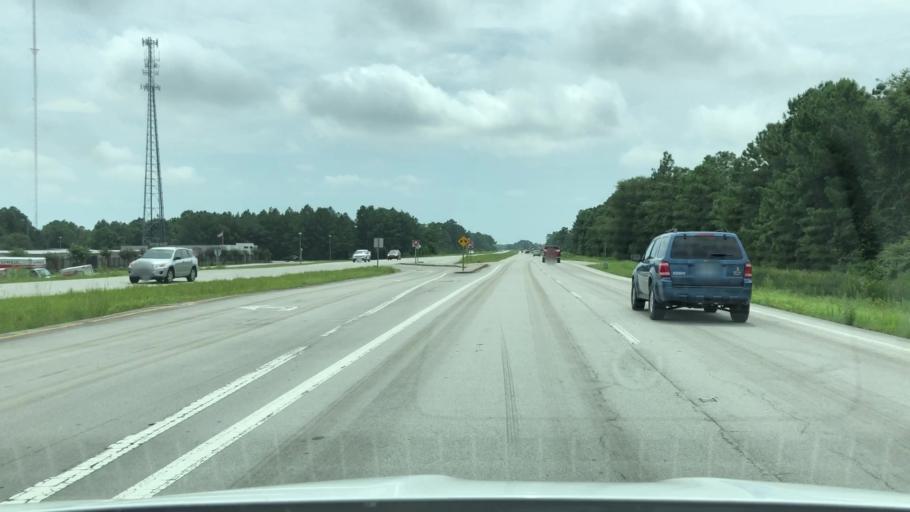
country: US
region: North Carolina
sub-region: Carteret County
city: Newport
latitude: 34.8031
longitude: -76.8787
